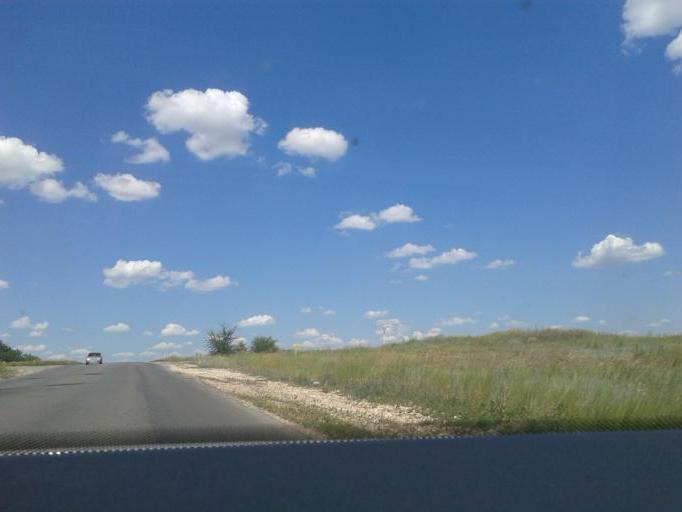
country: RU
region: Volgograd
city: Frolovo
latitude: 49.6713
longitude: 43.6303
